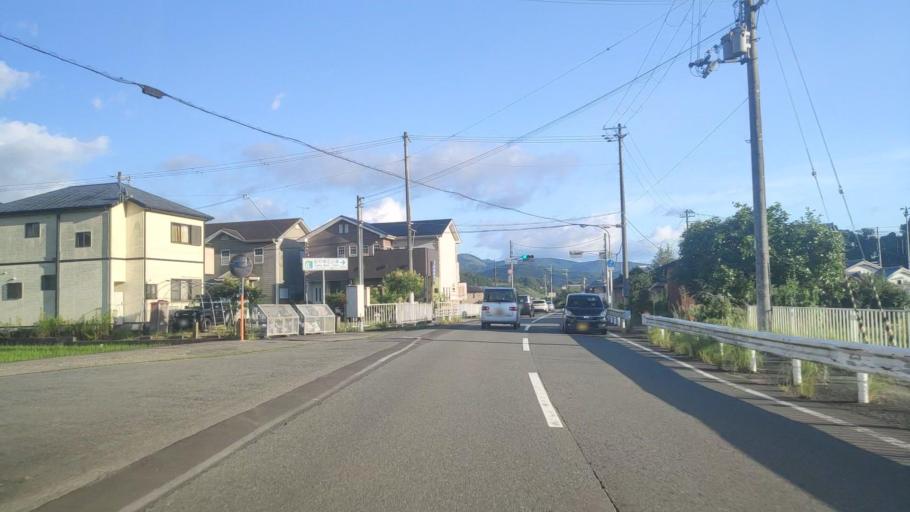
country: JP
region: Wakayama
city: Tanabe
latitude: 33.7212
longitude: 135.4456
